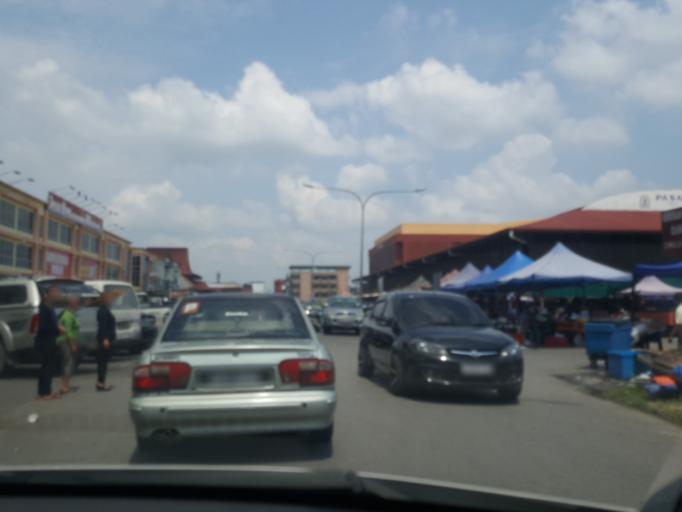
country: MY
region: Sarawak
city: Sarikei
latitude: 2.1333
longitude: 111.5247
